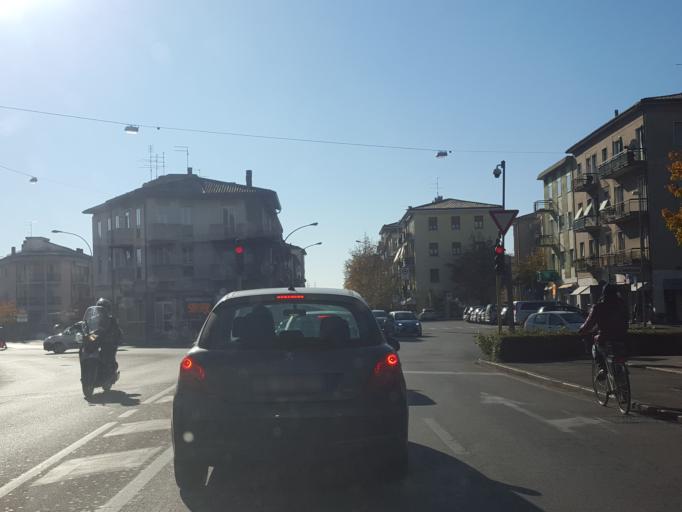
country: IT
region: Veneto
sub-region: Provincia di Verona
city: Verona
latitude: 45.4130
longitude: 10.9889
